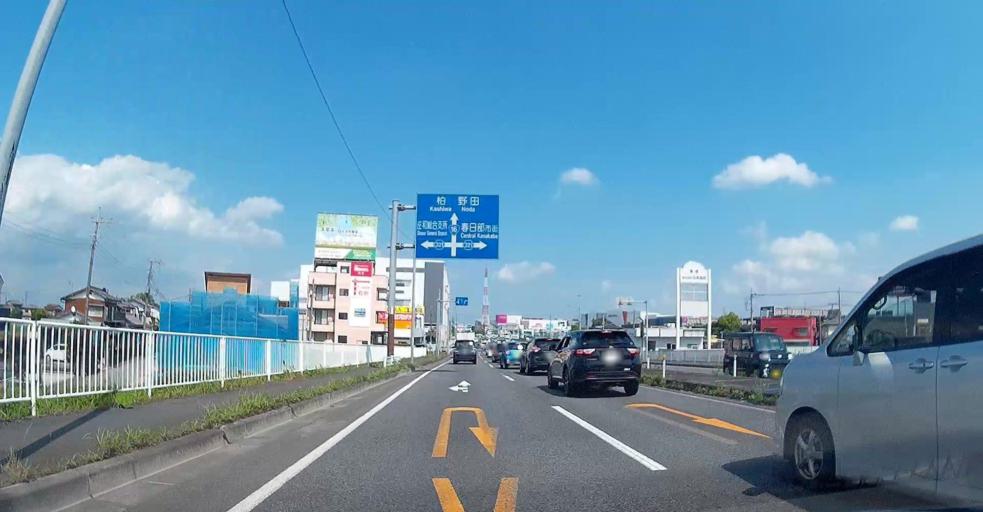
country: JP
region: Saitama
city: Kasukabe
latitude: 35.9905
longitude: 139.7824
